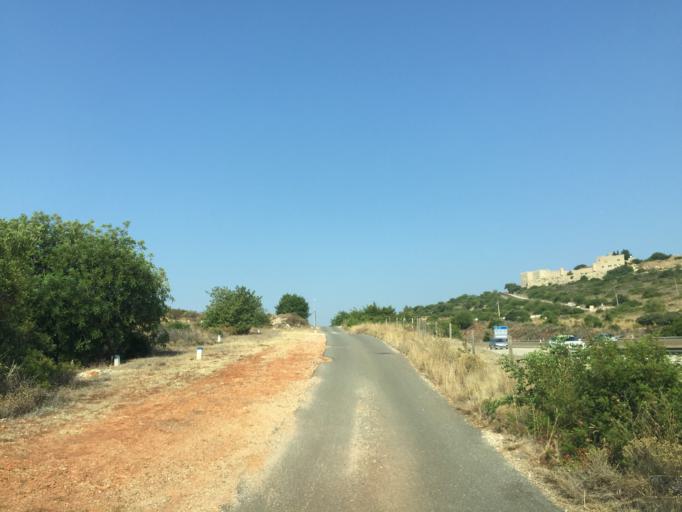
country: PT
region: Faro
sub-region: Loule
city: Almancil
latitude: 37.0989
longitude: -8.0054
